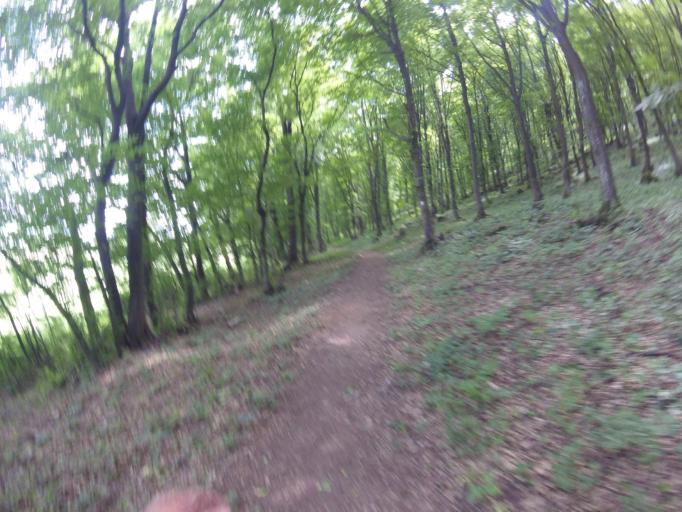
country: SK
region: Kosicky
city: Medzev
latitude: 48.6225
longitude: 20.8590
